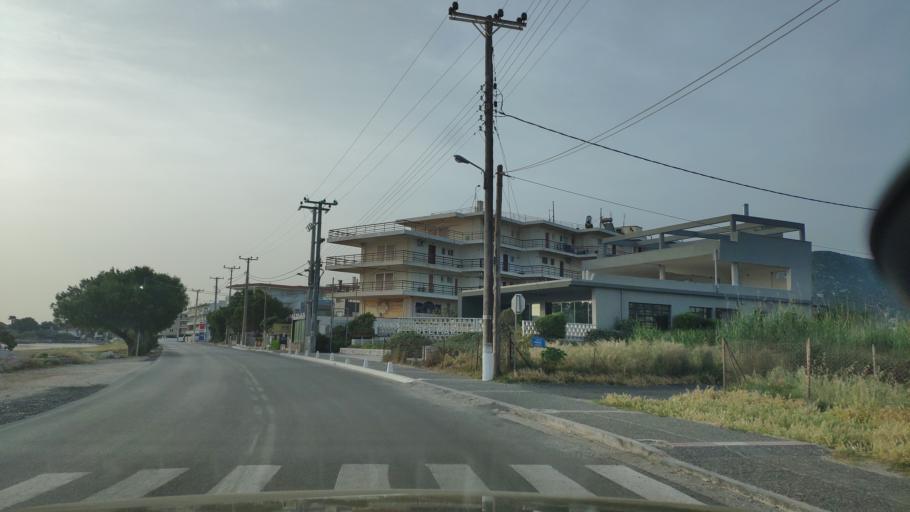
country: GR
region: Attica
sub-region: Nomarchia Anatolikis Attikis
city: Limin Mesoyaias
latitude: 37.8708
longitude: 24.0227
